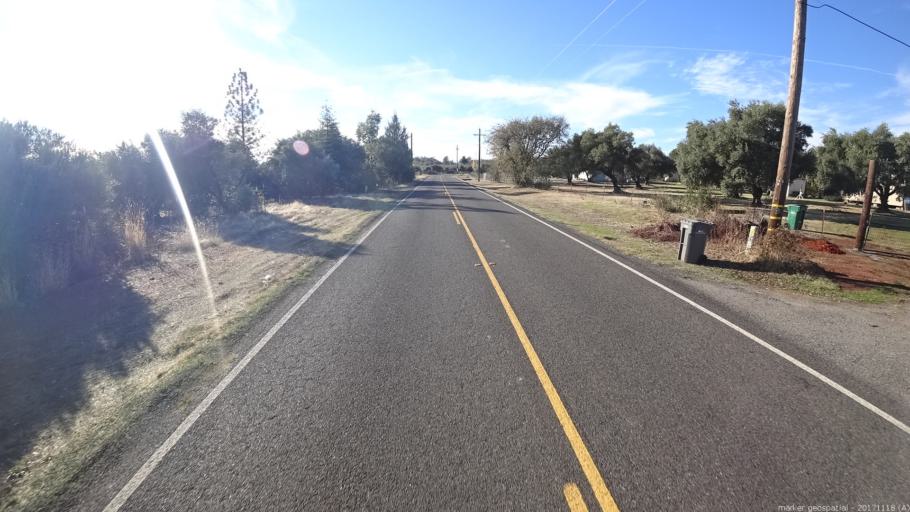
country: US
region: California
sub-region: Shasta County
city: Anderson
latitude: 40.4457
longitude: -122.4341
